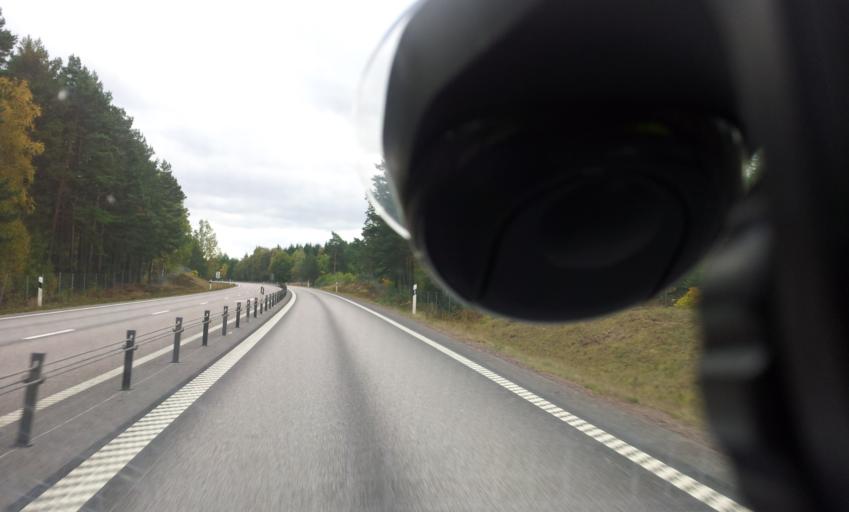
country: SE
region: Kalmar
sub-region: Oskarshamns Kommun
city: Paskallavik
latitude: 57.1611
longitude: 16.4467
